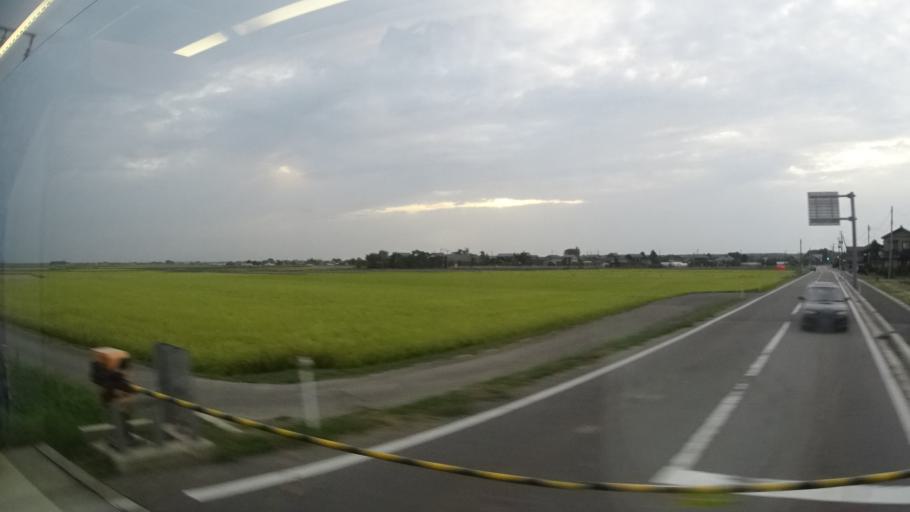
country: JP
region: Niigata
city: Murakami
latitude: 38.1724
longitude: 139.4596
